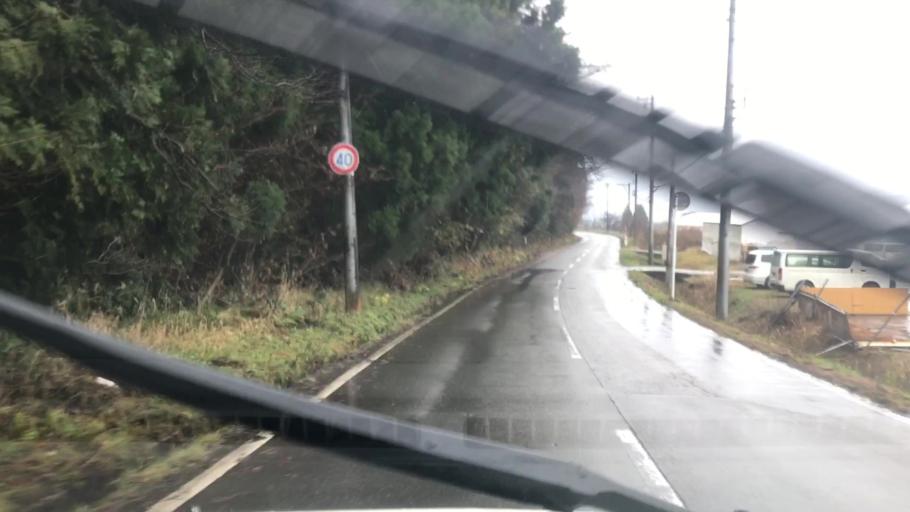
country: JP
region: Toyama
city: Toyama-shi
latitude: 36.6041
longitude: 137.2846
